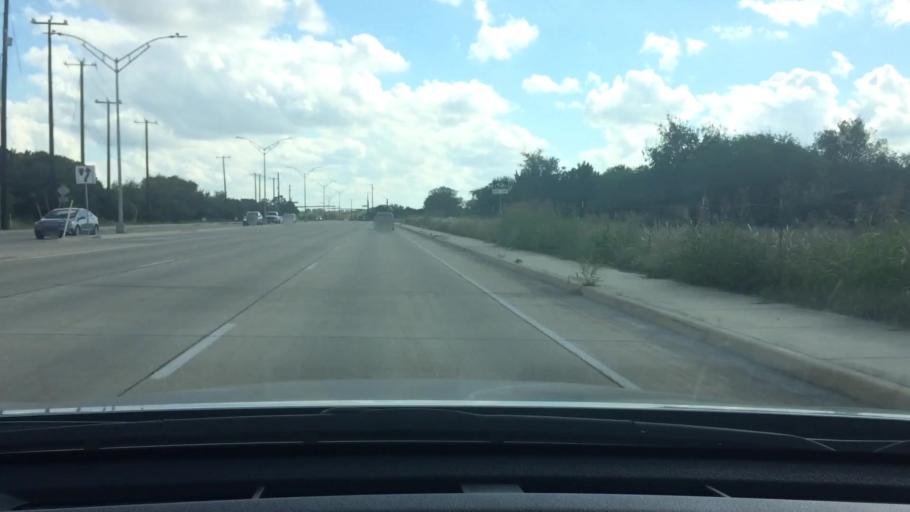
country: US
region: Texas
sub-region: Bexar County
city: Hollywood Park
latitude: 29.6197
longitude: -98.4230
